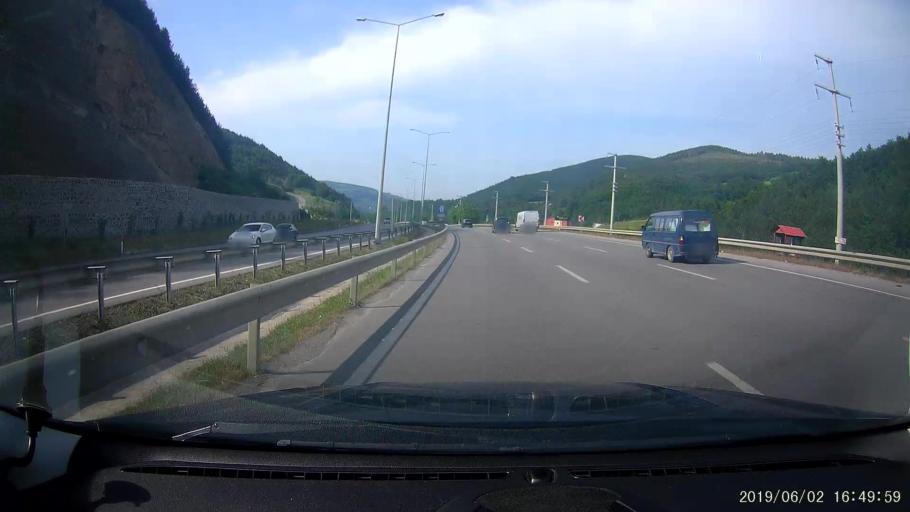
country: TR
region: Samsun
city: Samsun
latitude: 41.2452
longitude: 36.1722
